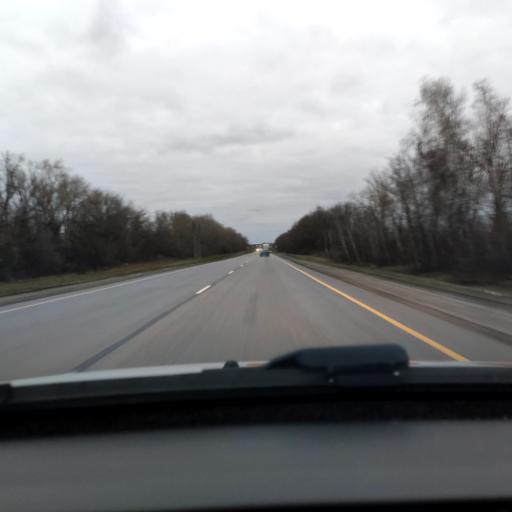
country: RU
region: Lipetsk
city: Borinskoye
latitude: 52.4128
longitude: 39.2483
